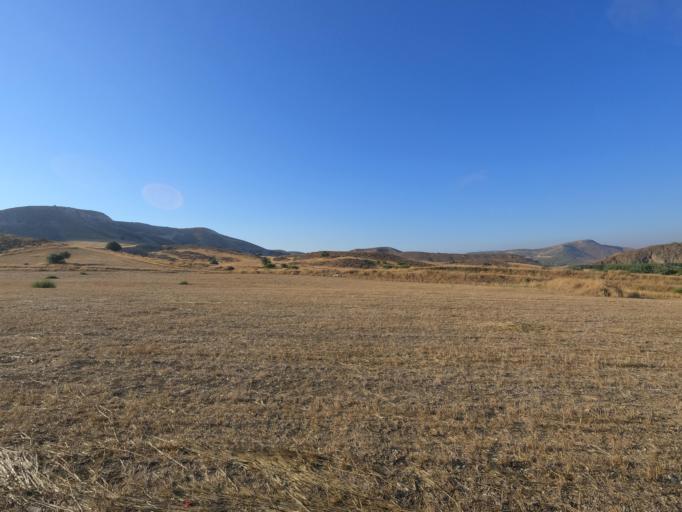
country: CY
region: Larnaka
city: Troulloi
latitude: 35.0227
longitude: 33.6467
